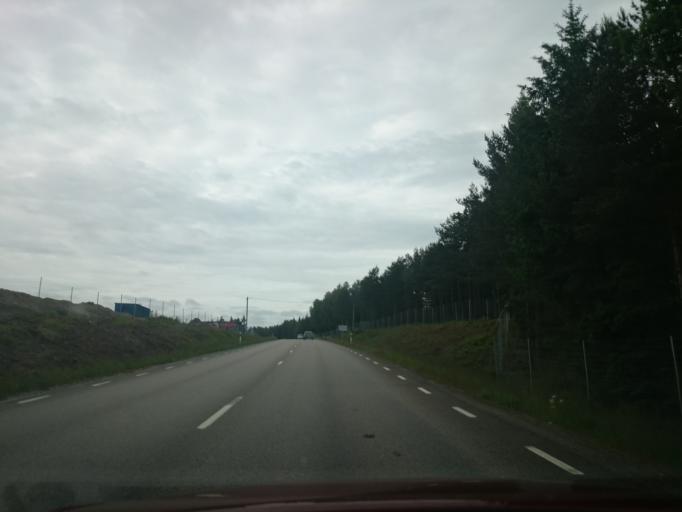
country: SE
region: Vaestra Goetaland
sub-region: Harryda Kommun
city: Hindas
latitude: 57.6815
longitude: 12.3605
